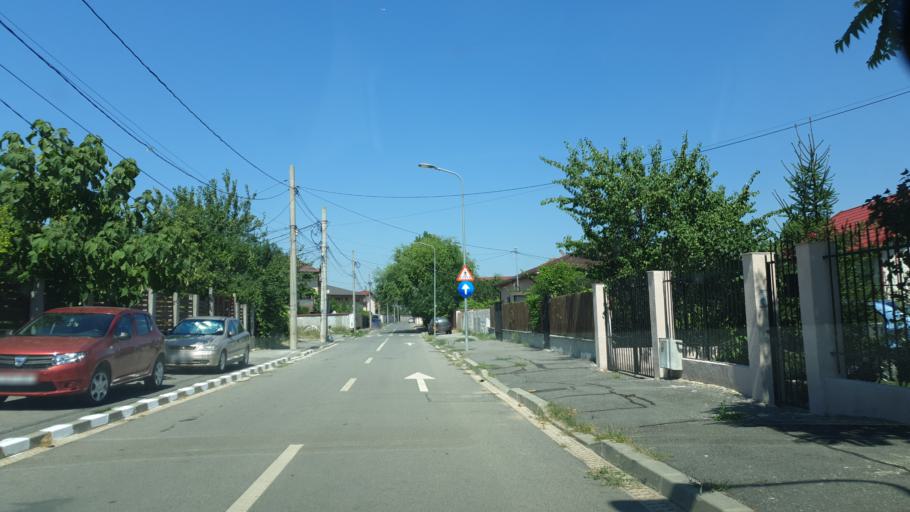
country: RO
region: Ilfov
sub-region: Comuna Chiajna
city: Rosu
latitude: 44.4643
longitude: 26.0210
